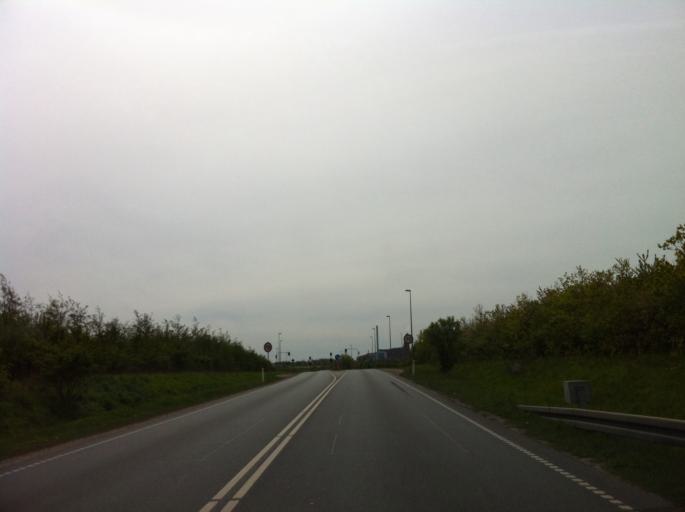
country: DK
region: Zealand
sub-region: Roskilde Kommune
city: Roskilde
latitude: 55.6645
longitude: 12.1166
